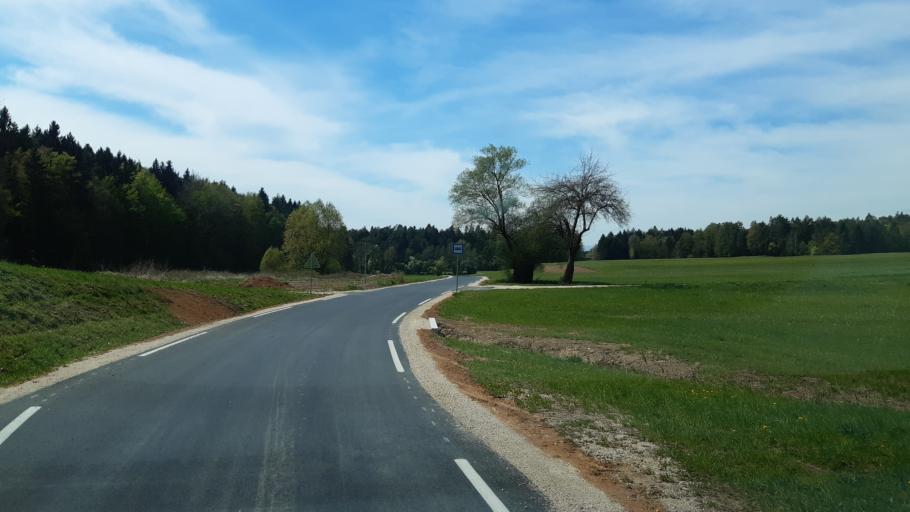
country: SI
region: Domzale
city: Dob
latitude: 46.1754
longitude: 14.6501
